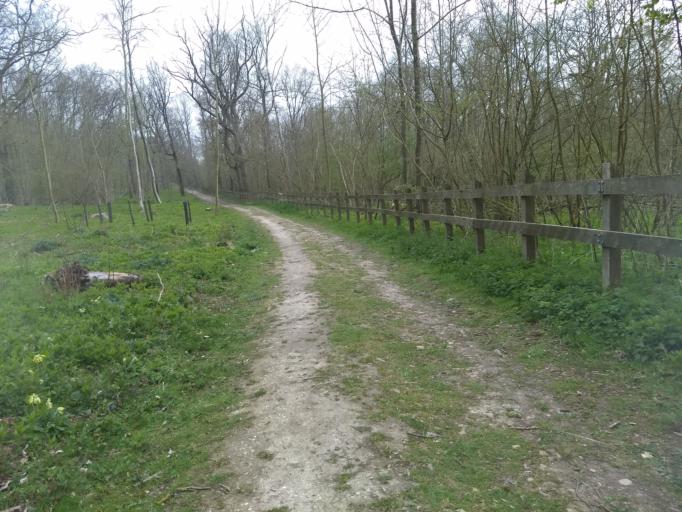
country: FR
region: Nord-Pas-de-Calais
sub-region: Departement du Pas-de-Calais
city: Maroeuil
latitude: 50.3319
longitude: 2.6940
